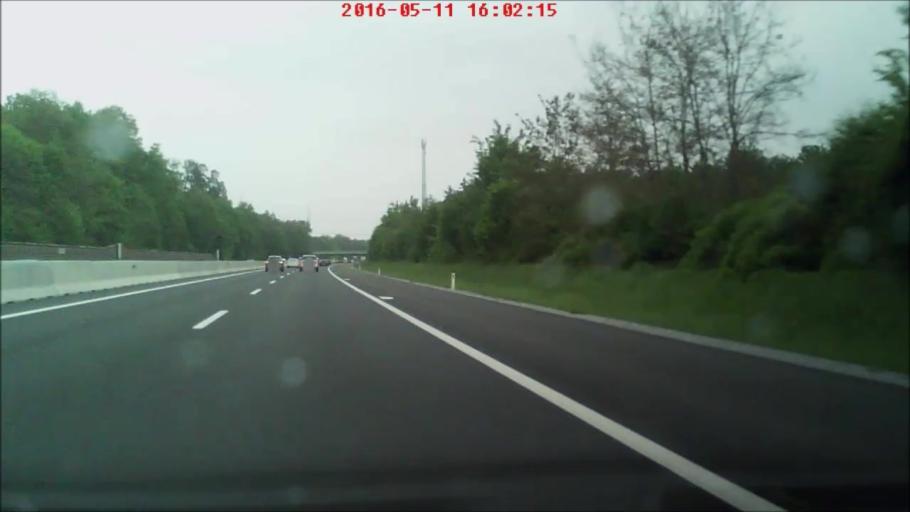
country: AT
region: Styria
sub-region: Politischer Bezirk Graz-Umgebung
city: Wundschuh
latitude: 46.9190
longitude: 15.4705
